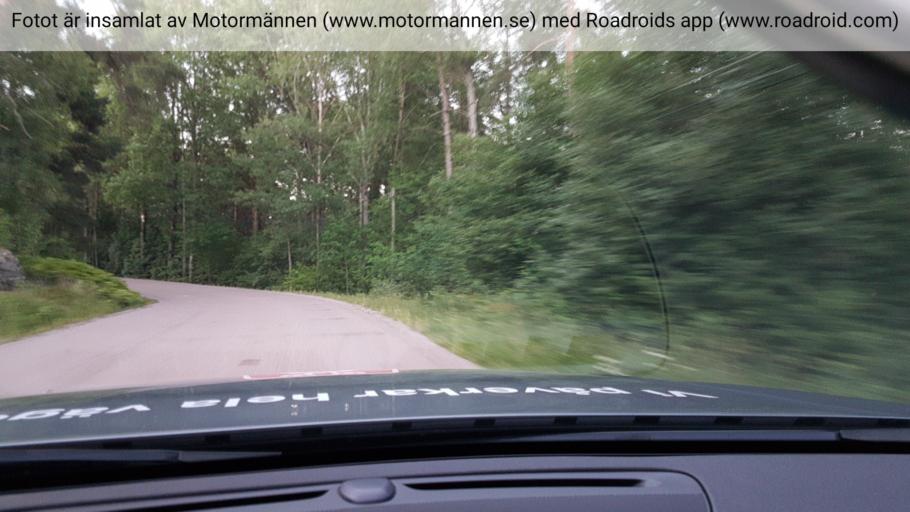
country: SE
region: Vaestmanland
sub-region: Hallstahammars Kommun
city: Kolback
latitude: 59.5227
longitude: 16.1984
